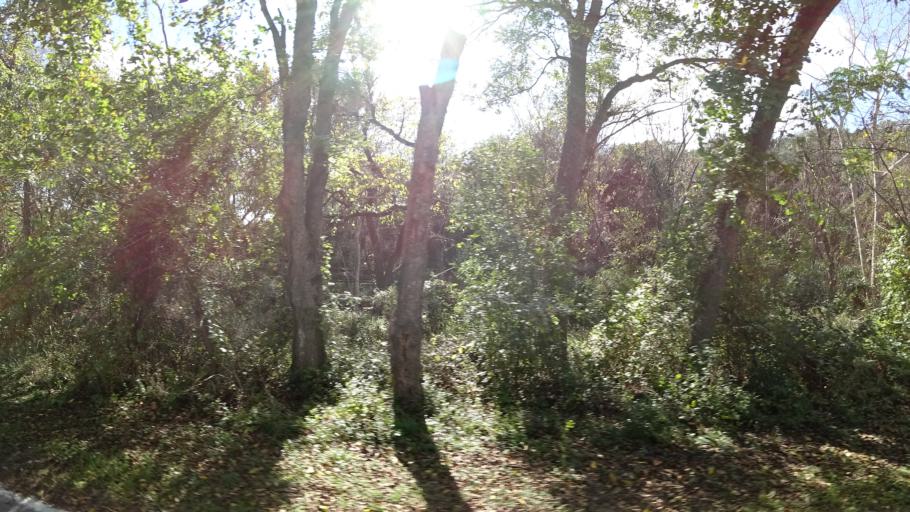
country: US
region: Texas
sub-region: Williamson County
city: Jollyville
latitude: 30.3976
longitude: -97.7803
